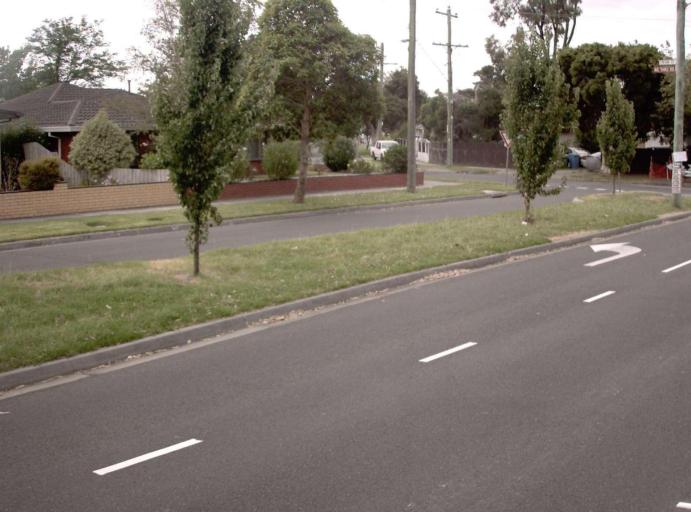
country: AU
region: Victoria
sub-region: Greater Dandenong
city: Dandenong North
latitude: -37.9633
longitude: 145.2247
